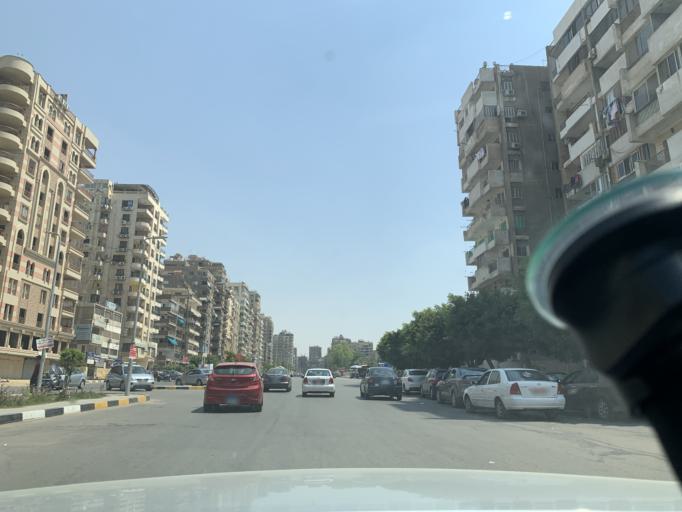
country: EG
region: Muhafazat al Qahirah
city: Cairo
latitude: 30.0660
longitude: 31.3490
